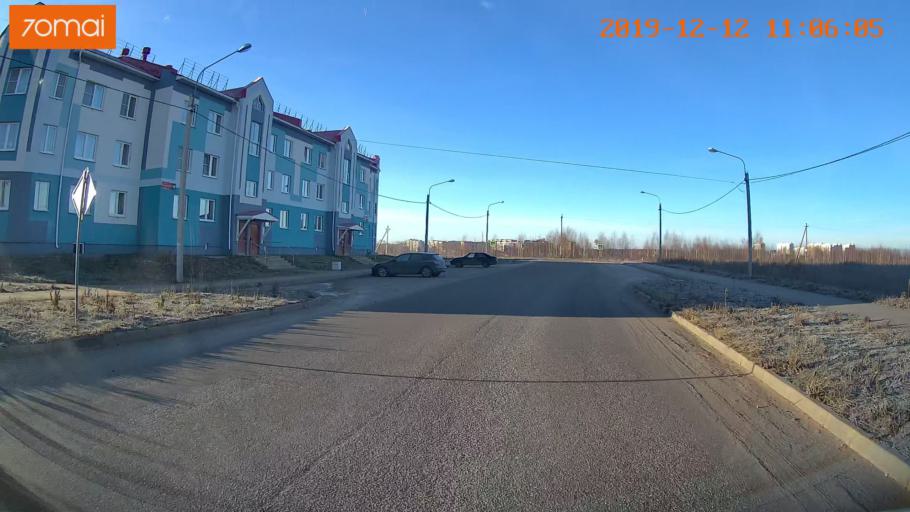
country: RU
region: Ivanovo
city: Kokhma
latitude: 56.9452
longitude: 41.0895
